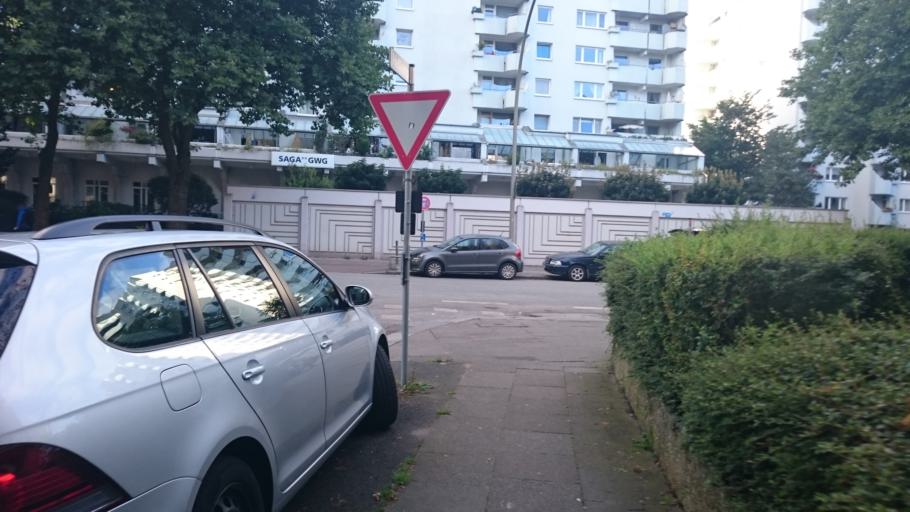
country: DE
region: Hamburg
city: Stellingen
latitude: 53.5822
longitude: 9.9498
